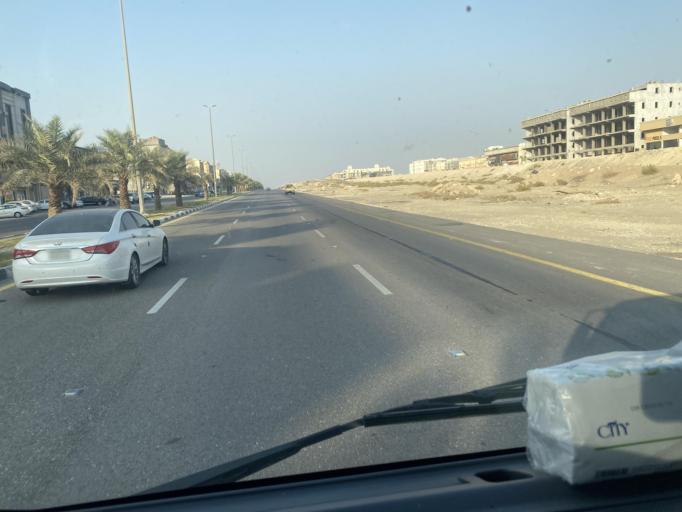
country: SA
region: Eastern Province
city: Dhahran
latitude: 26.3571
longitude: 50.0617
